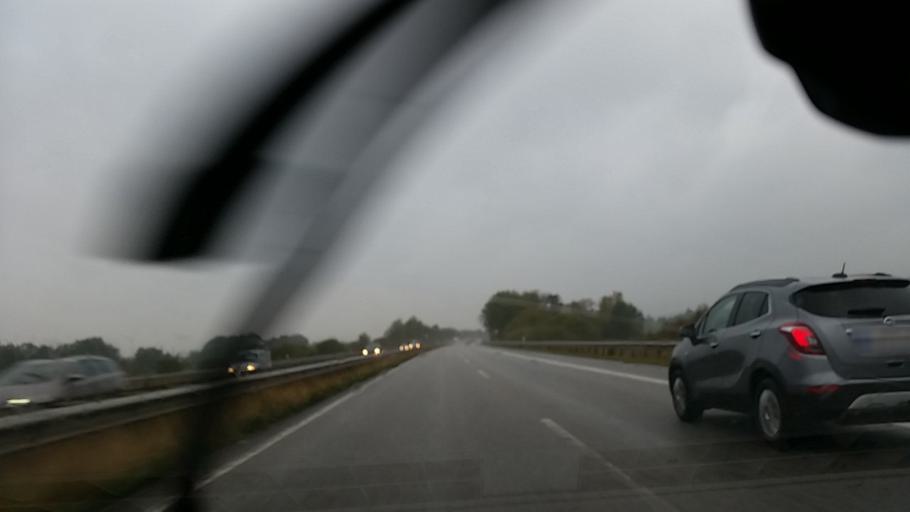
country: DE
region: Schleswig-Holstein
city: Escheburg
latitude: 53.4581
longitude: 10.3010
